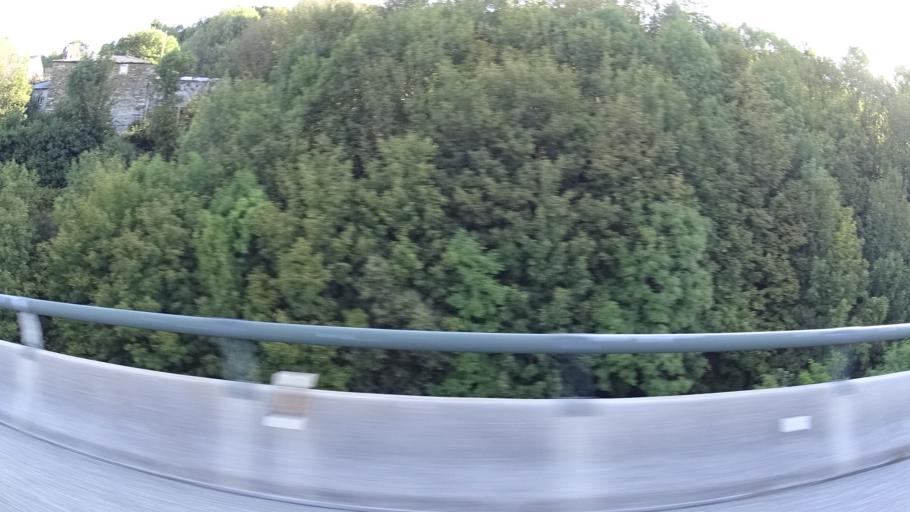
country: ES
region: Galicia
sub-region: Provincia de Lugo
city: San Roman
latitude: 42.7574
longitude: -7.0745
